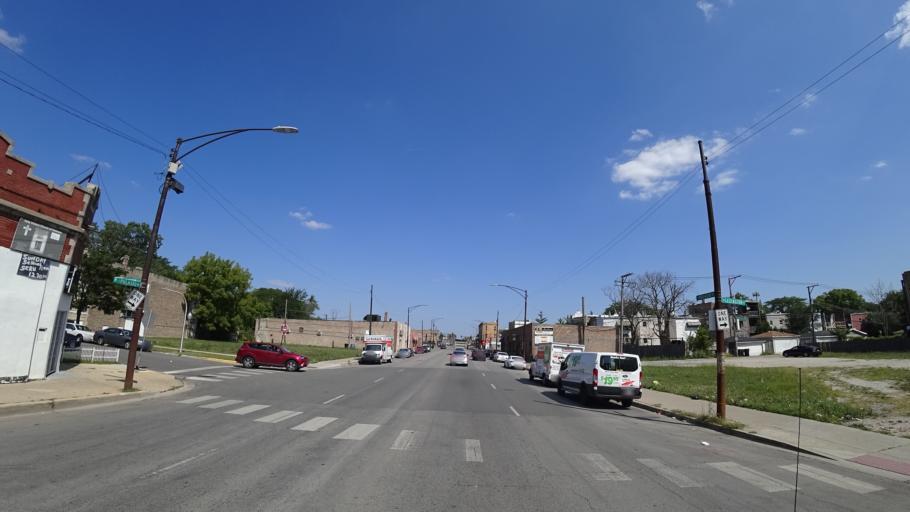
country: US
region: Illinois
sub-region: Cook County
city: Cicero
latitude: 41.8717
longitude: -87.7253
